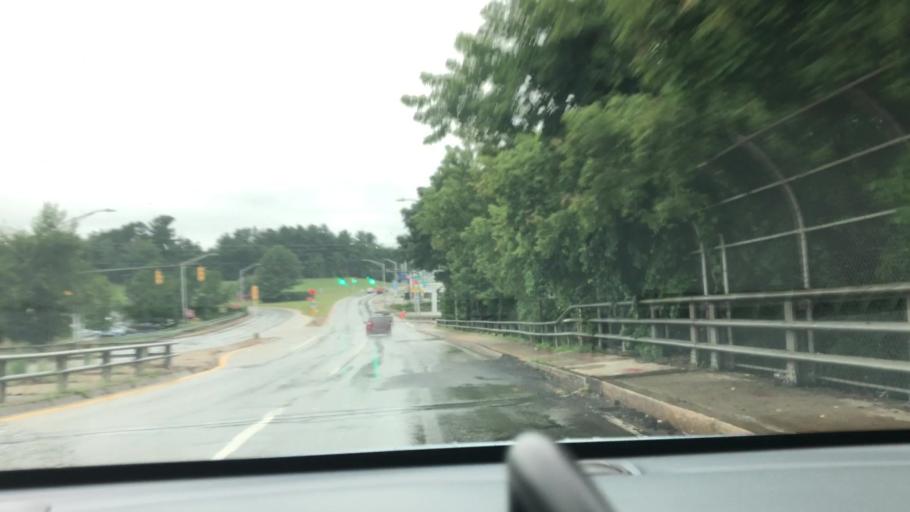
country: US
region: New Hampshire
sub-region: Hillsborough County
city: Manchester
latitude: 43.0042
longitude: -71.4709
